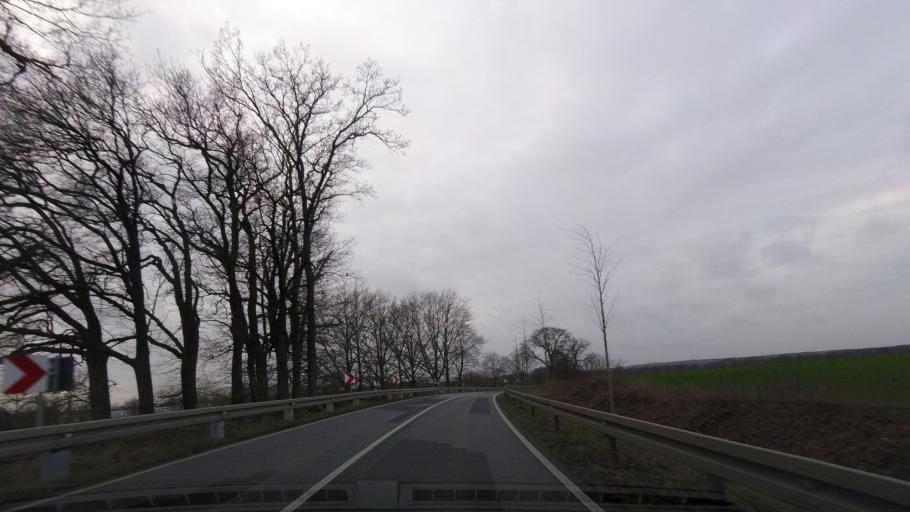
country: DE
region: Mecklenburg-Vorpommern
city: Robel
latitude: 53.3607
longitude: 12.5121
